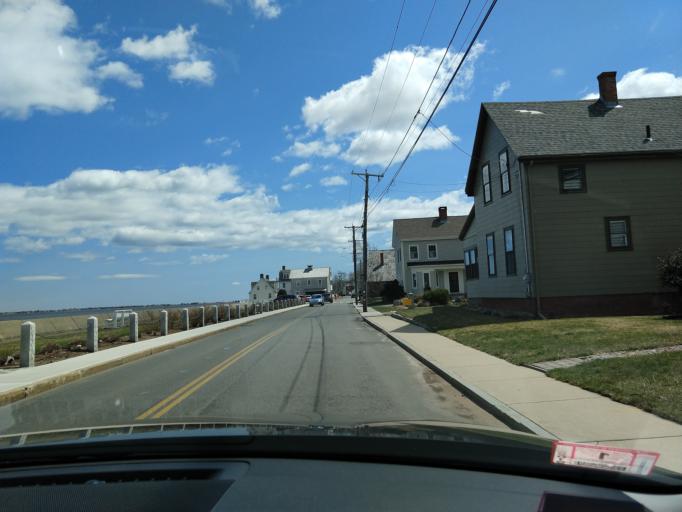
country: US
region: Massachusetts
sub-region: Essex County
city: Newburyport
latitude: 42.8069
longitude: -70.8587
